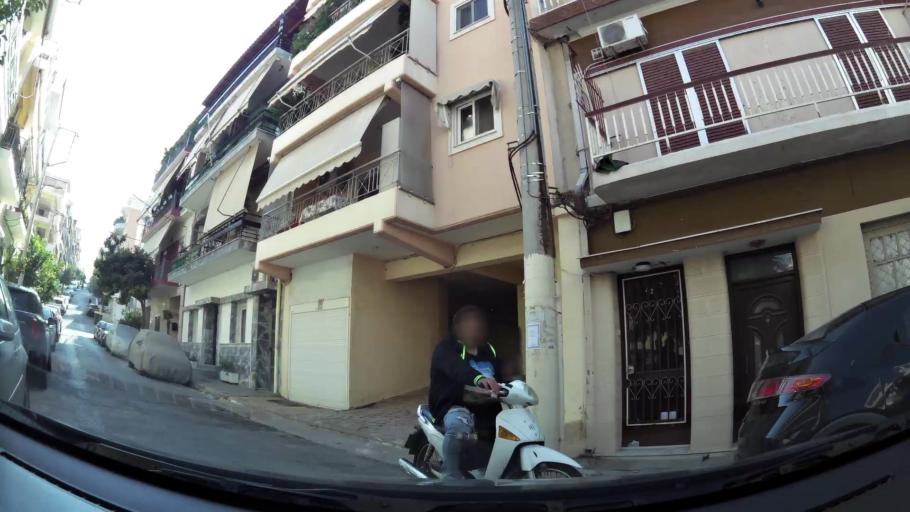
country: GR
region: Attica
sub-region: Nomos Piraios
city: Keratsini
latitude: 37.9582
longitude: 23.6168
